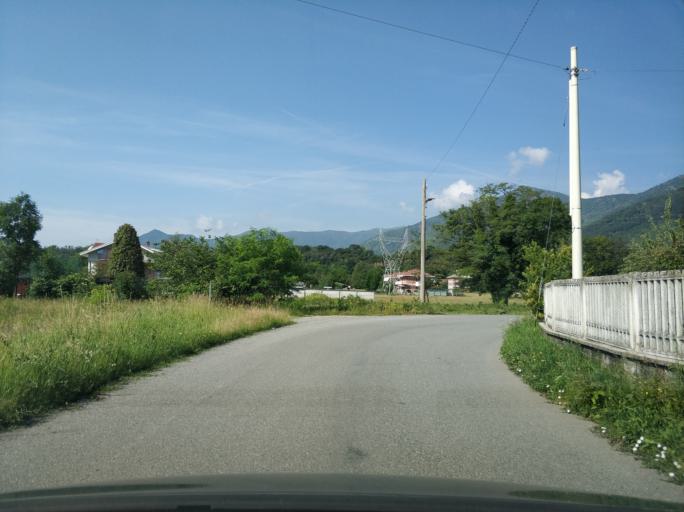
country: IT
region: Piedmont
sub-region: Provincia di Torino
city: Cafasse
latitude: 45.2429
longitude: 7.5254
